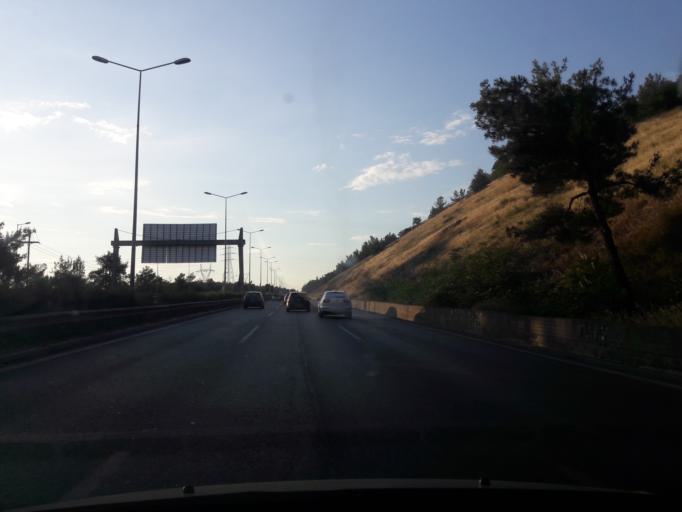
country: GR
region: Central Macedonia
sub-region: Nomos Thessalonikis
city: Agios Pavlos
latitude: 40.6340
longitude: 22.9730
